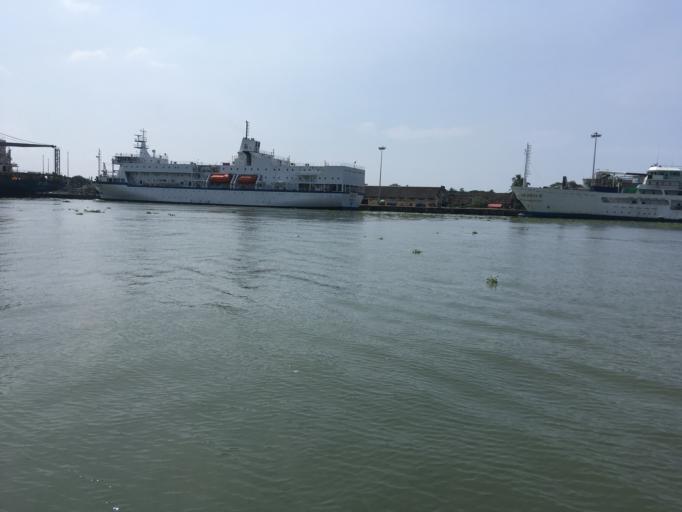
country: IN
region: Kerala
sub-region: Ernakulam
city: Cochin
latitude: 9.9698
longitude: 76.2674
